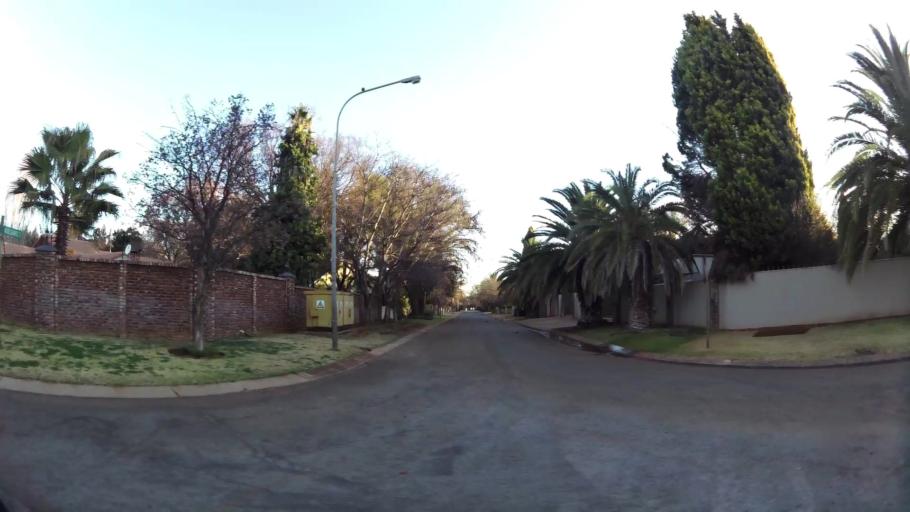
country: ZA
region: North-West
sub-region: Dr Kenneth Kaunda District Municipality
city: Potchefstroom
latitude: -26.6778
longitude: 27.1109
